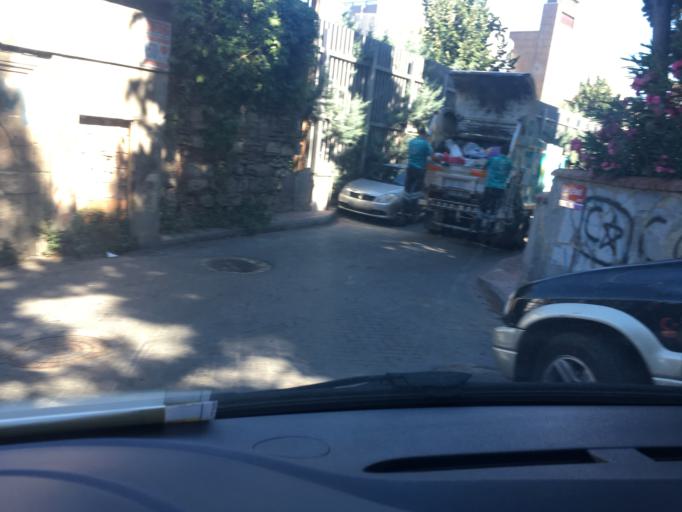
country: TR
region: Istanbul
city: Istanbul
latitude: 41.0487
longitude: 28.9413
